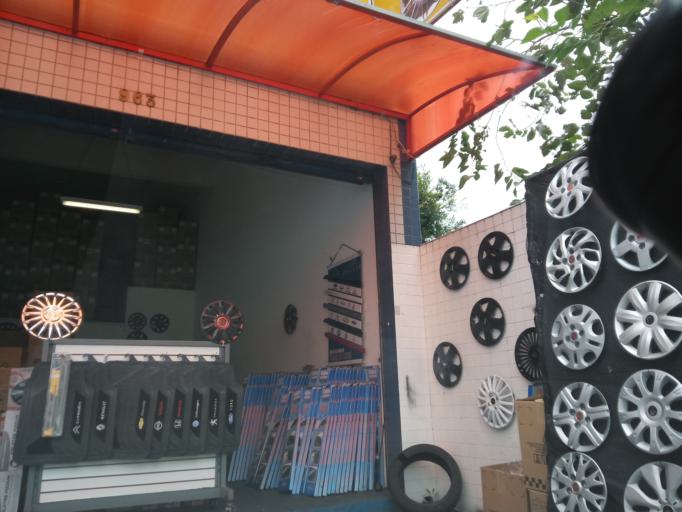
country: BR
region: Sao Paulo
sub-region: Sao Bernardo Do Campo
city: Sao Bernardo do Campo
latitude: -23.7206
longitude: -46.5726
